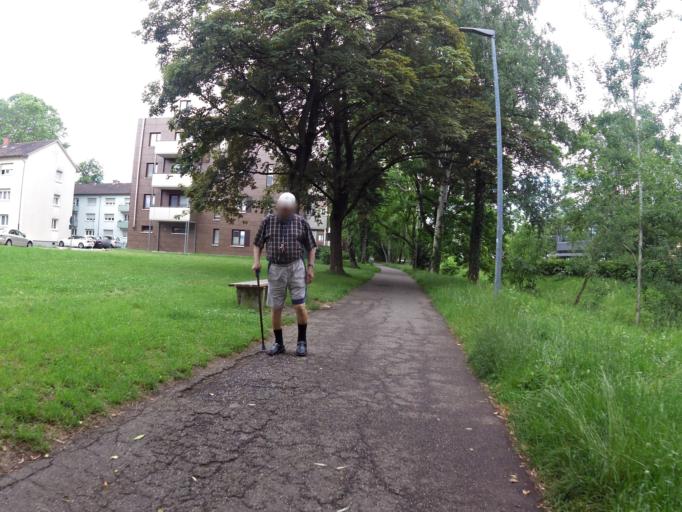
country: DE
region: Baden-Wuerttemberg
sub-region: Freiburg Region
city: Lahr
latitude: 48.3405
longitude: 7.8486
